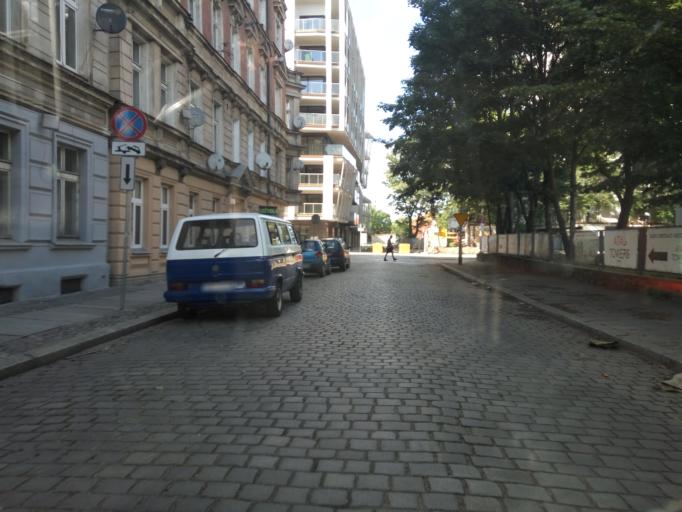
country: PL
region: Lower Silesian Voivodeship
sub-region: Powiat wroclawski
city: Wroclaw
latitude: 51.1133
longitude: 17.0210
